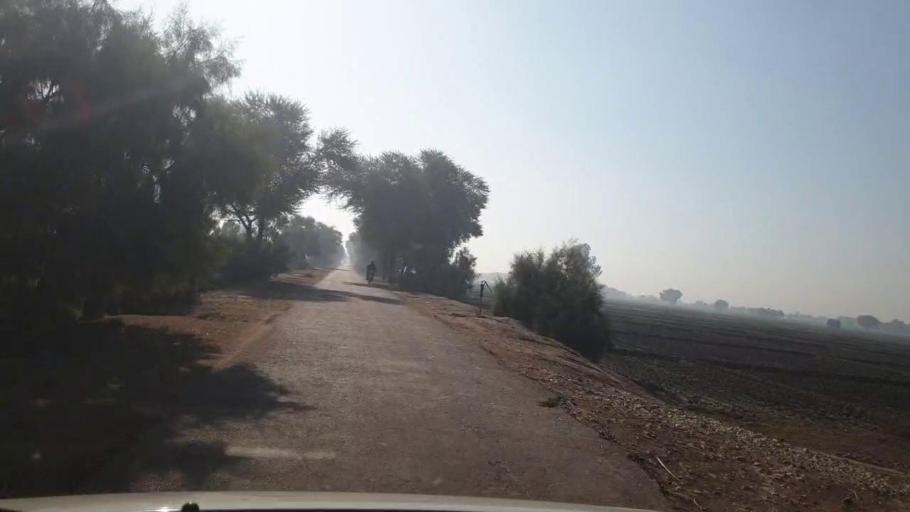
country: PK
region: Sindh
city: Dadu
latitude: 26.6642
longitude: 67.8179
